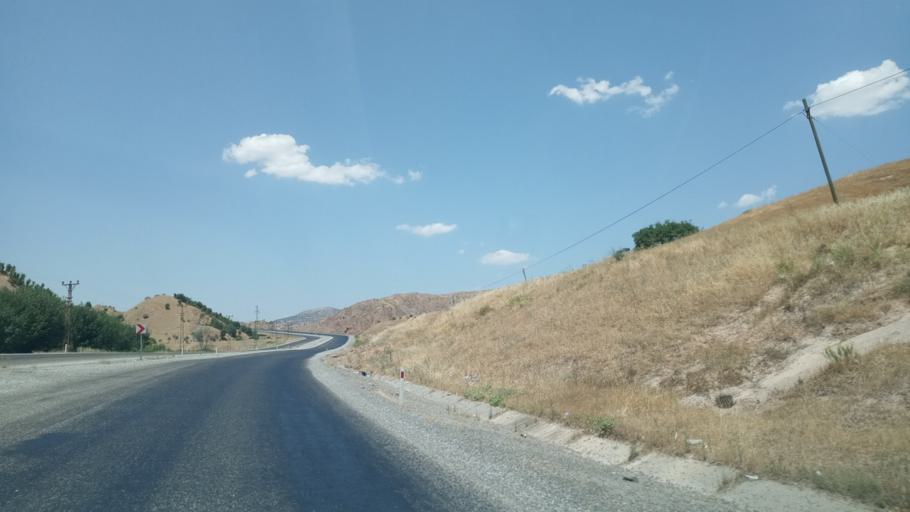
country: TR
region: Batman
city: Kozluk
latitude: 38.1703
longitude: 41.4538
